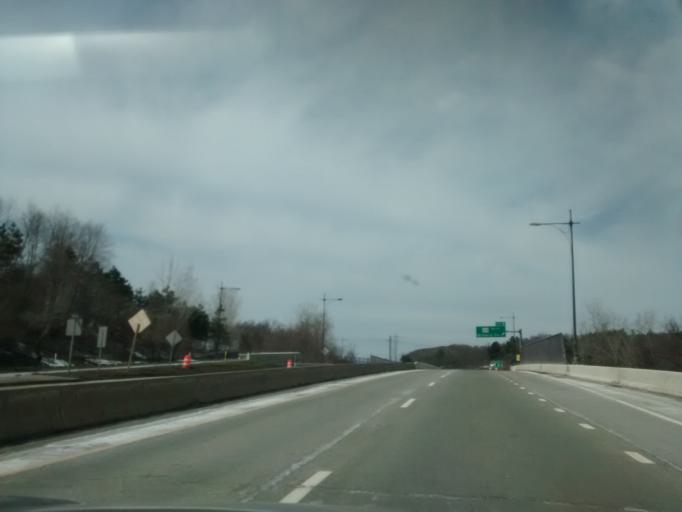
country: US
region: Massachusetts
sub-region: Worcester County
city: Millbury
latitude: 42.1981
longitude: -71.7740
